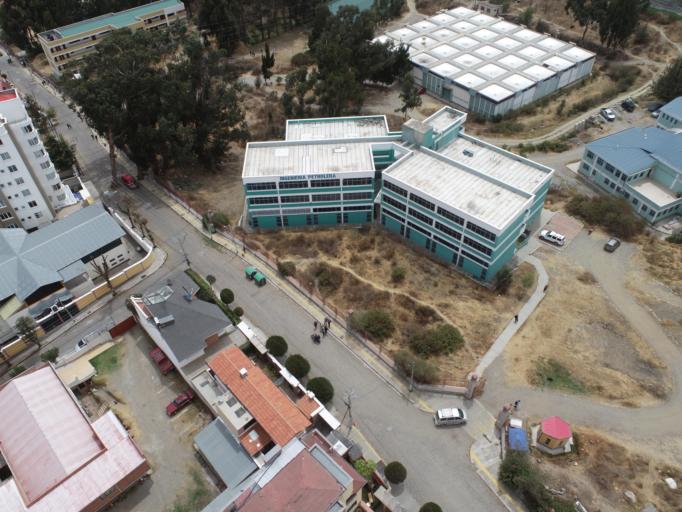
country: BO
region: La Paz
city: La Paz
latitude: -16.5396
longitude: -68.0626
